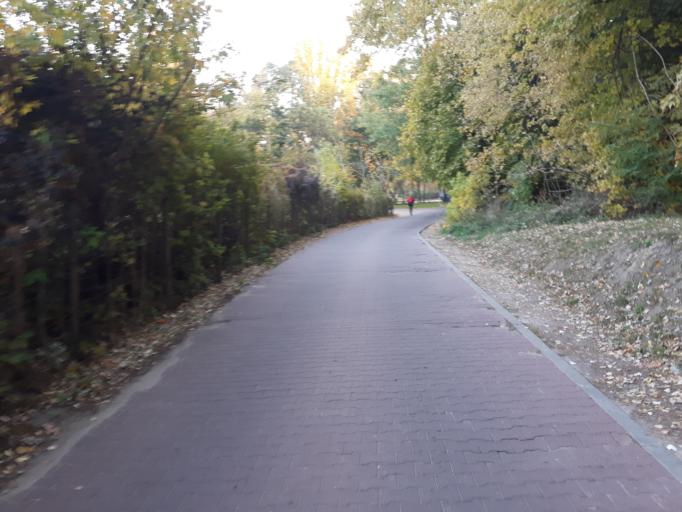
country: PL
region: Masovian Voivodeship
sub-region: Warszawa
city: Ochota
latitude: 52.2120
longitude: 20.9914
